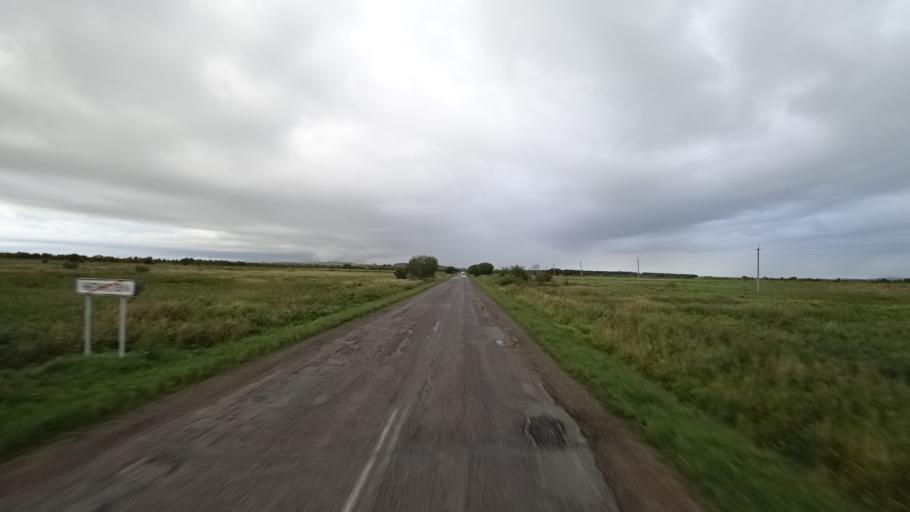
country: RU
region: Primorskiy
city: Chernigovka
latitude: 44.3570
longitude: 132.5610
